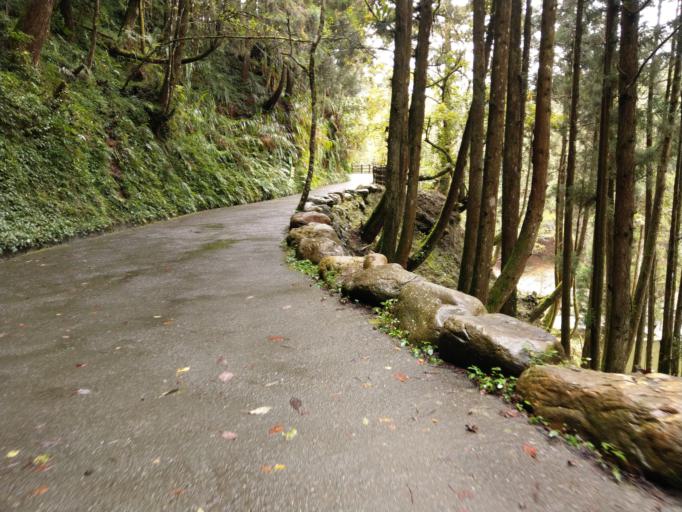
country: TW
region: Taiwan
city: Lugu
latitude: 23.6386
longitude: 120.7874
